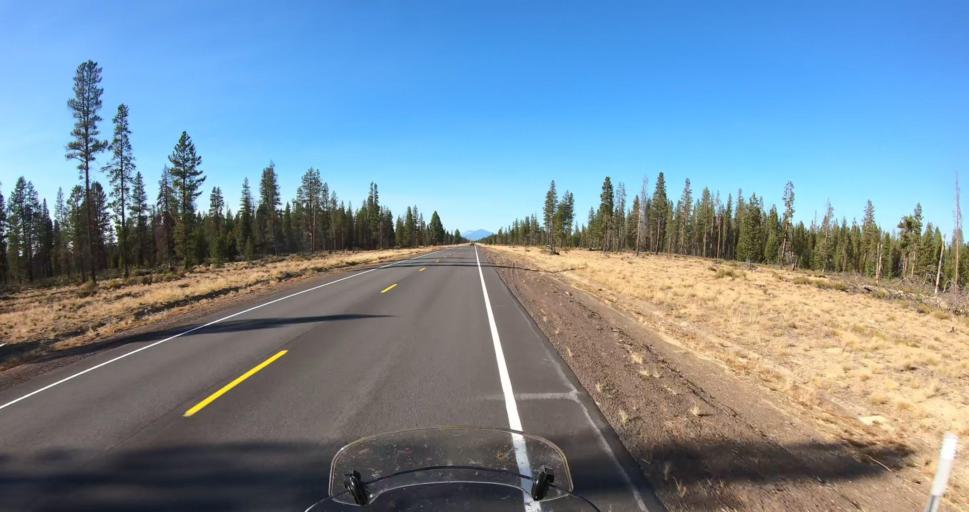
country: US
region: Oregon
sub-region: Deschutes County
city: La Pine
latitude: 43.5691
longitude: -121.4812
